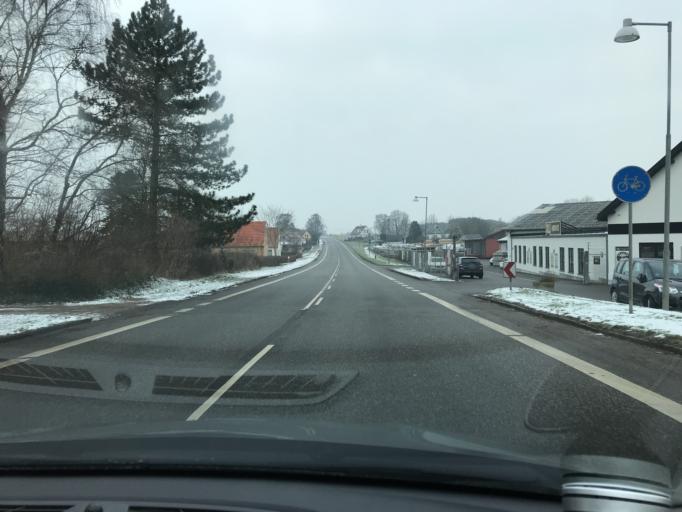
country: DK
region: Zealand
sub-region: Odsherred Kommune
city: Horve
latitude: 55.7558
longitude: 11.4540
